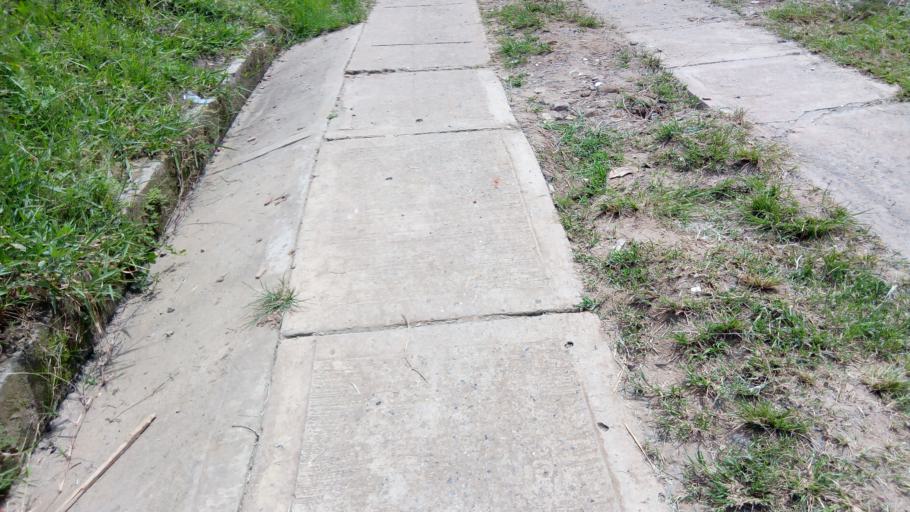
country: CO
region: Valle del Cauca
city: Cali
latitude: 3.3830
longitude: -76.5640
